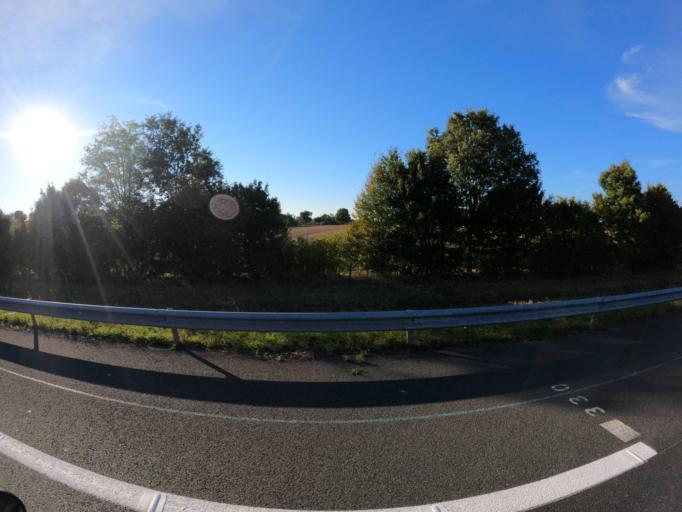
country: FR
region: Pays de la Loire
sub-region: Departement de Maine-et-Loire
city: Chemille-Melay
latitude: 47.2030
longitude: -0.7701
